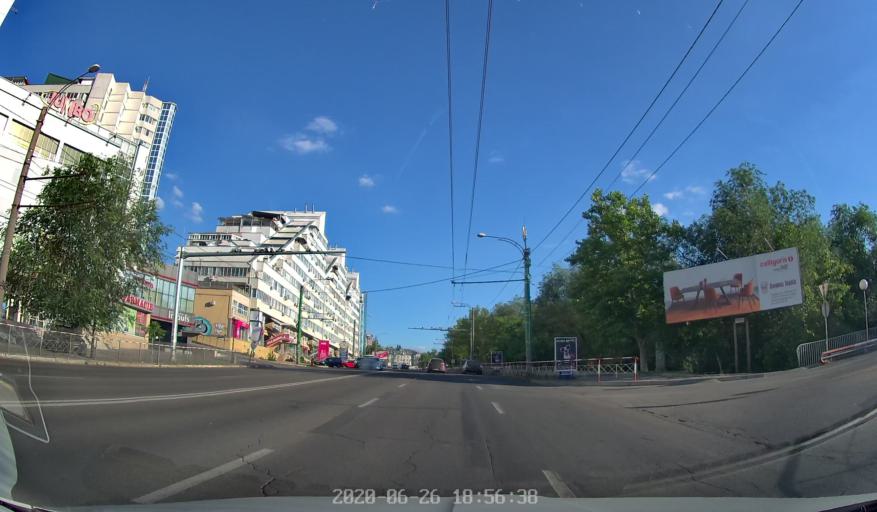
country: MD
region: Chisinau
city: Chisinau
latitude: 47.0043
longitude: 28.8595
